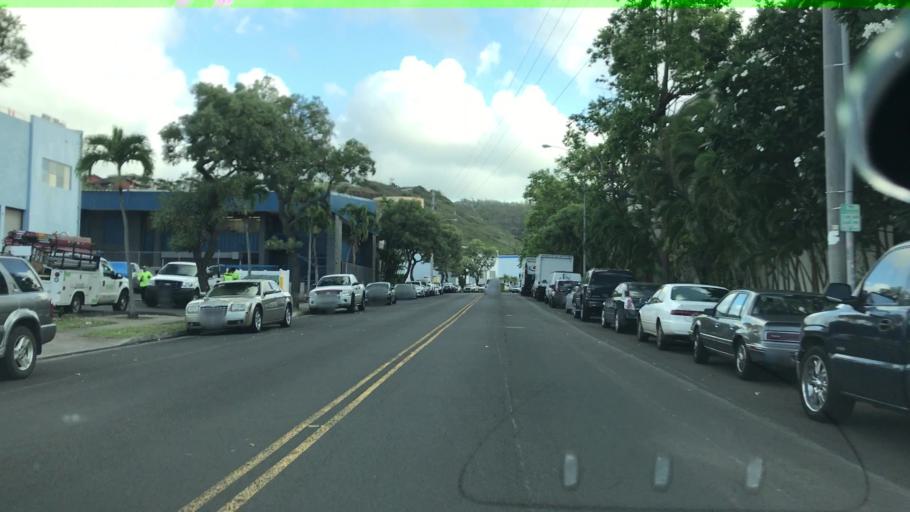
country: US
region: Hawaii
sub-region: Honolulu County
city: Halawa Heights
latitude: 21.3728
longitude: -157.9136
